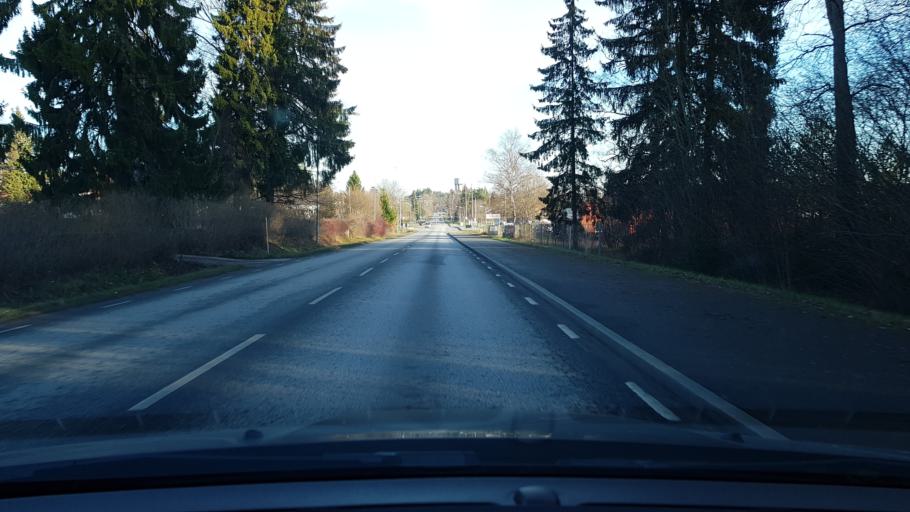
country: SE
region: Stockholm
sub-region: Norrtalje Kommun
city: Rimbo
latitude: 59.7403
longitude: 18.3420
